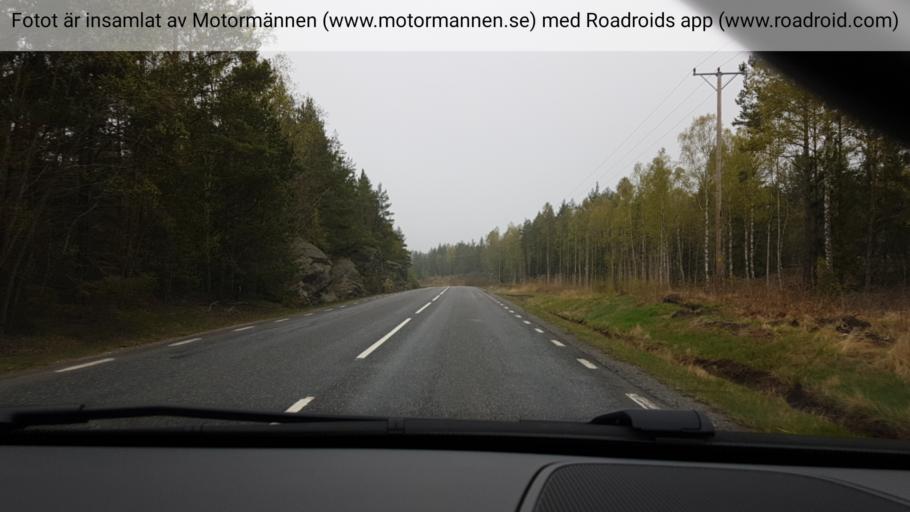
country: SE
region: Stockholm
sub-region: Nynashamns Kommun
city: Nynashamn
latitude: 58.9580
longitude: 17.9965
